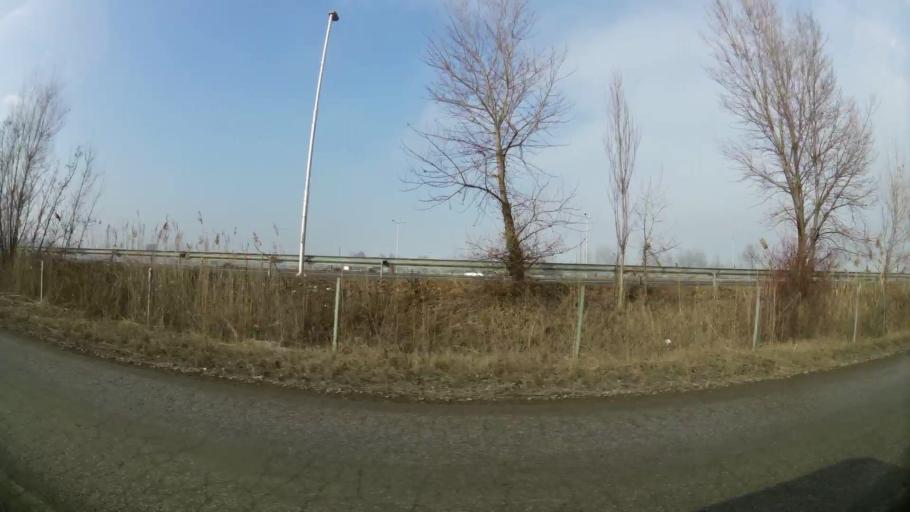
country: MK
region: Ilinden
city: Jurumleri
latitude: 41.9937
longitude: 21.5389
